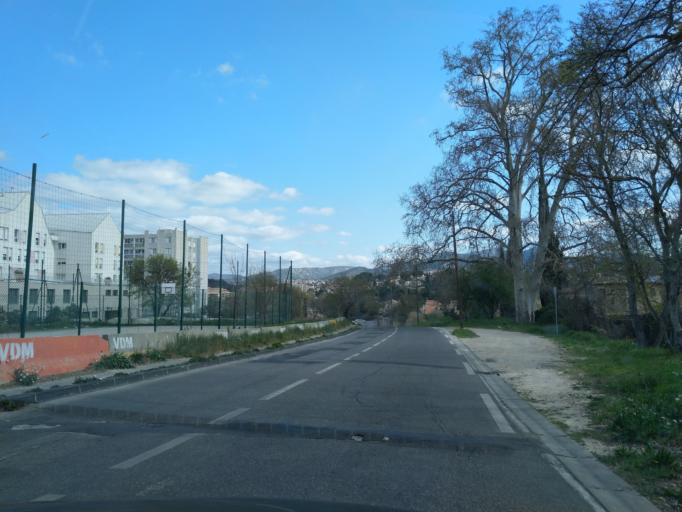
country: FR
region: Provence-Alpes-Cote d'Azur
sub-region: Departement des Bouches-du-Rhone
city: Plan-de-Cuques
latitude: 43.3286
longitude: 5.4553
